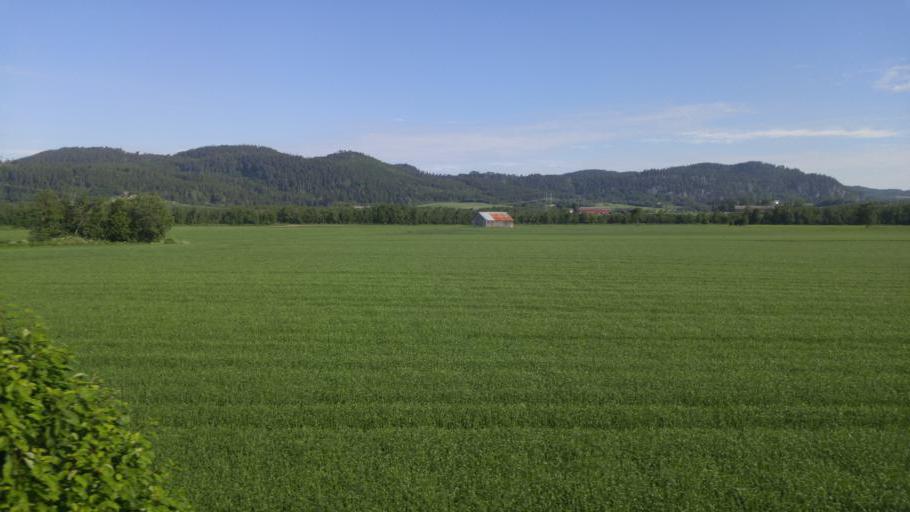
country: NO
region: Nord-Trondelag
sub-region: Stjordal
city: Stjordalshalsen
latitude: 63.4522
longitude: 11.0298
